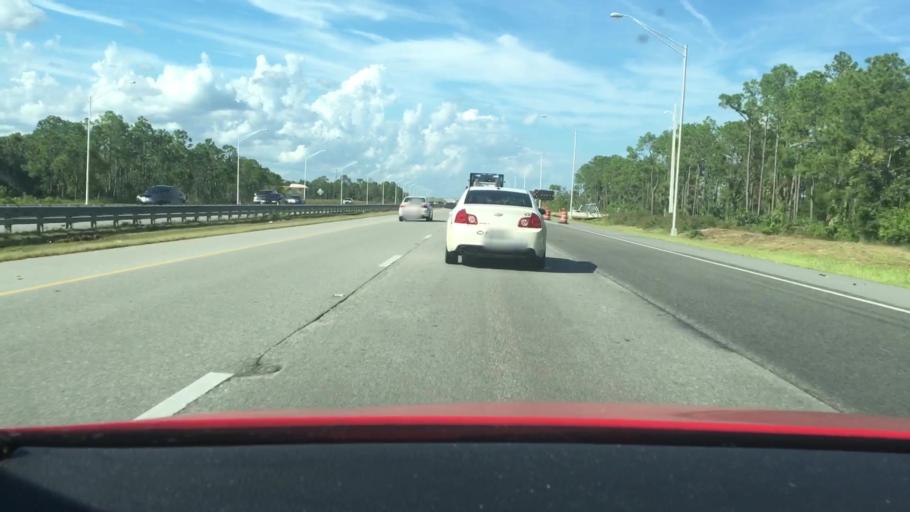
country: US
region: Florida
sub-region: Volusia County
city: South Daytona
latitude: 29.1420
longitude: -81.0678
